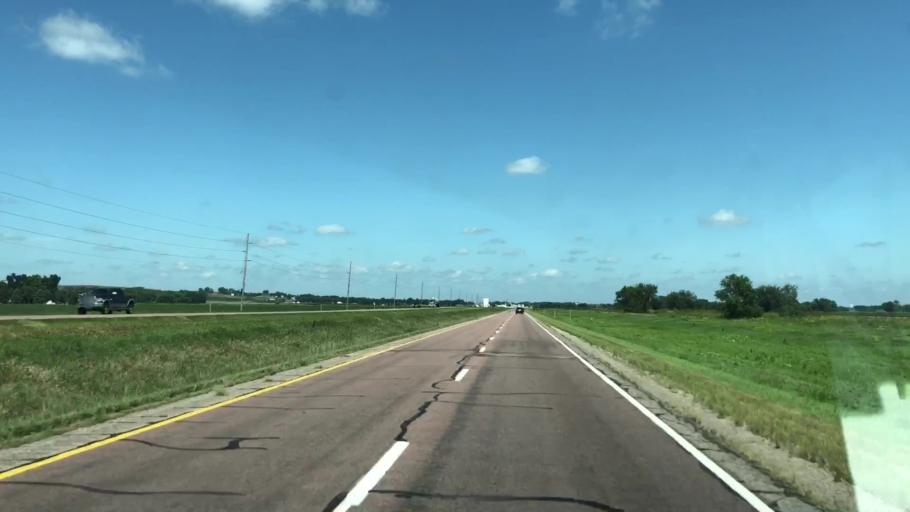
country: US
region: Iowa
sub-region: Plymouth County
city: Le Mars
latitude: 42.6942
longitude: -96.2610
